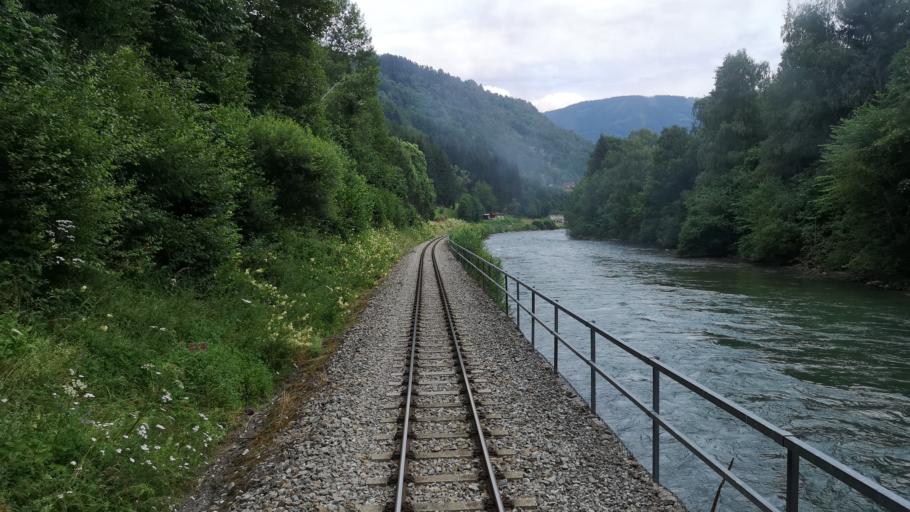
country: AT
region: Salzburg
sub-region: Politischer Bezirk Tamsweg
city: Ramingstein
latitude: 47.0718
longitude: 13.8716
